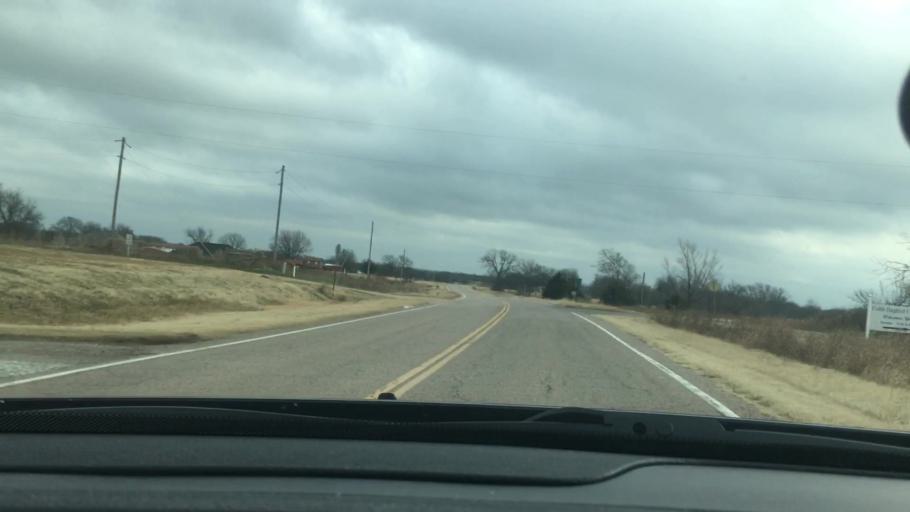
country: US
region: Oklahoma
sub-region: Bryan County
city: Durant
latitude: 34.0847
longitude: -96.4084
